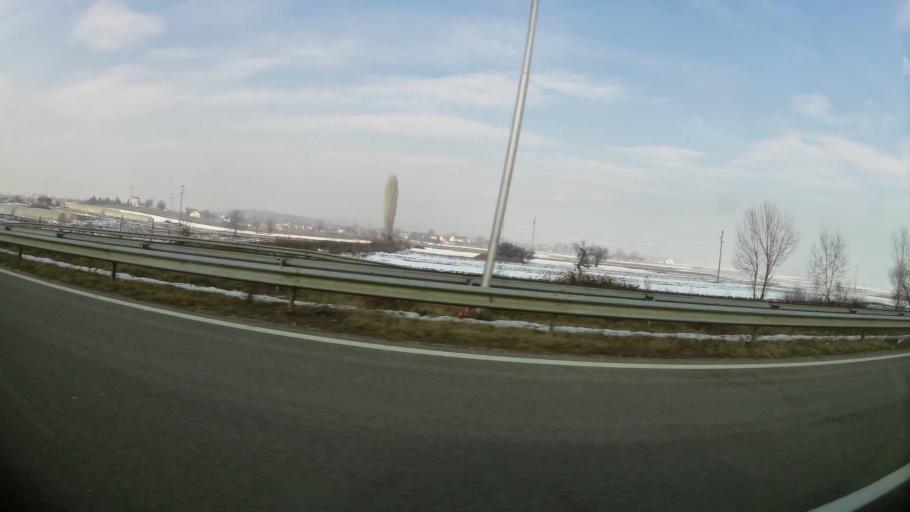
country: MK
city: Creshevo
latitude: 42.0324
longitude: 21.4951
